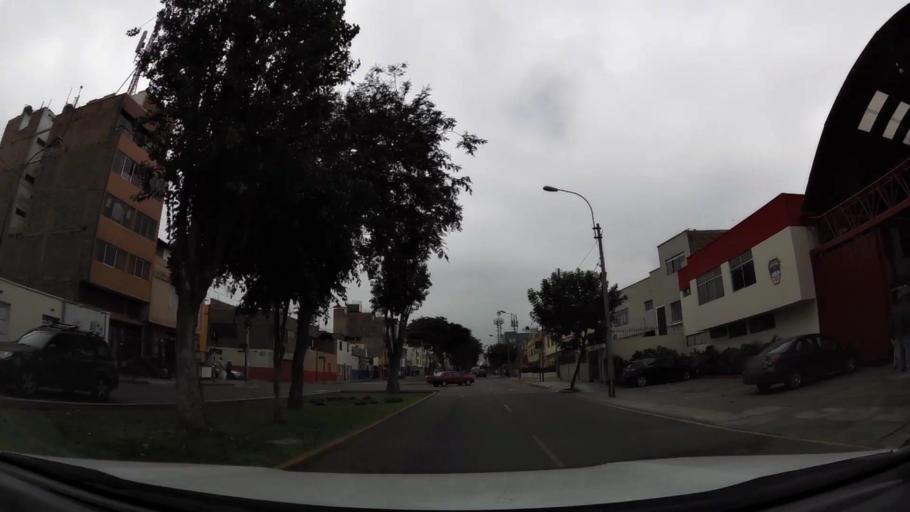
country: PE
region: Lima
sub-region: Lima
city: Surco
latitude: -12.1198
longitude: -77.0226
